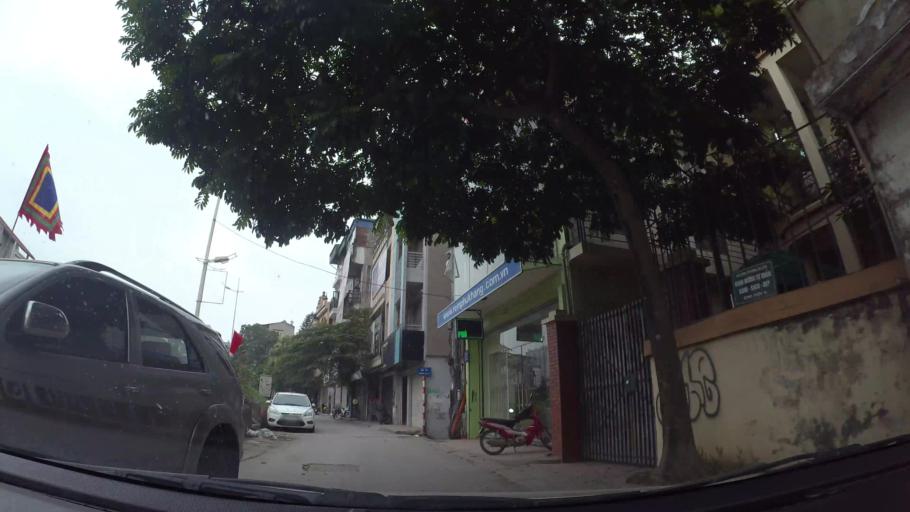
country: VN
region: Ha Noi
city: Tay Ho
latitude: 21.0650
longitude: 105.8324
